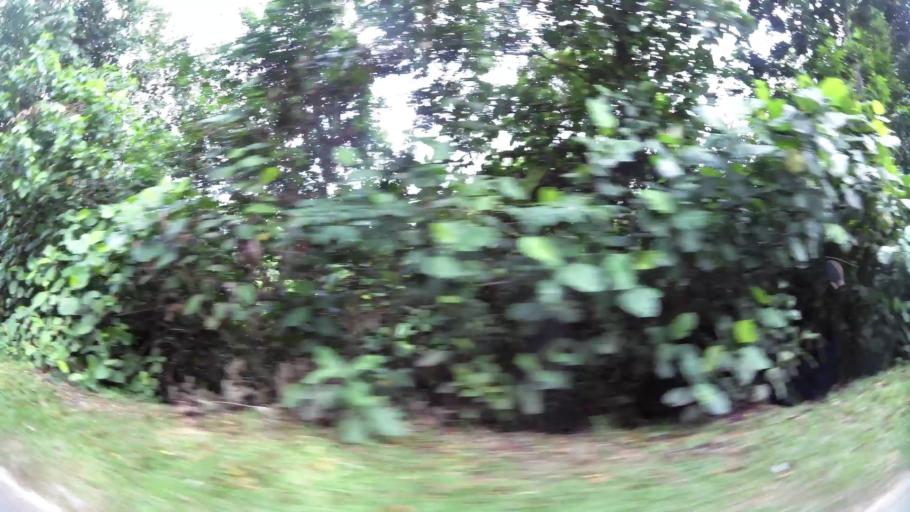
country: MY
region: Johor
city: Johor Bahru
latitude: 1.4141
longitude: 103.6998
